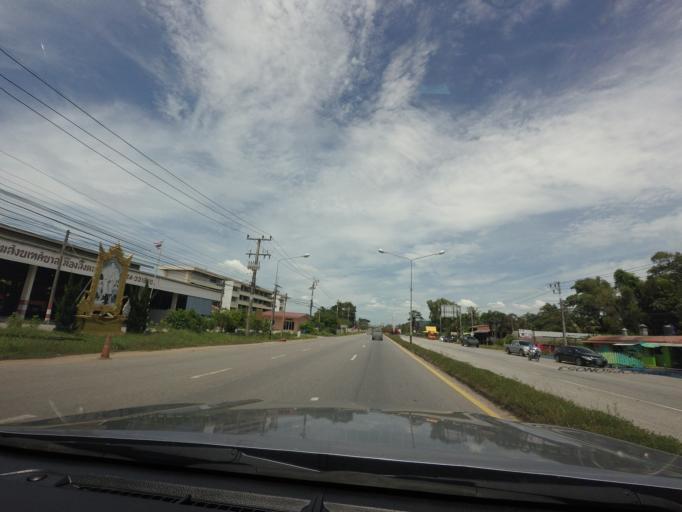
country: TH
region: Songkhla
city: Singhanakhon
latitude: 7.2419
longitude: 100.5455
